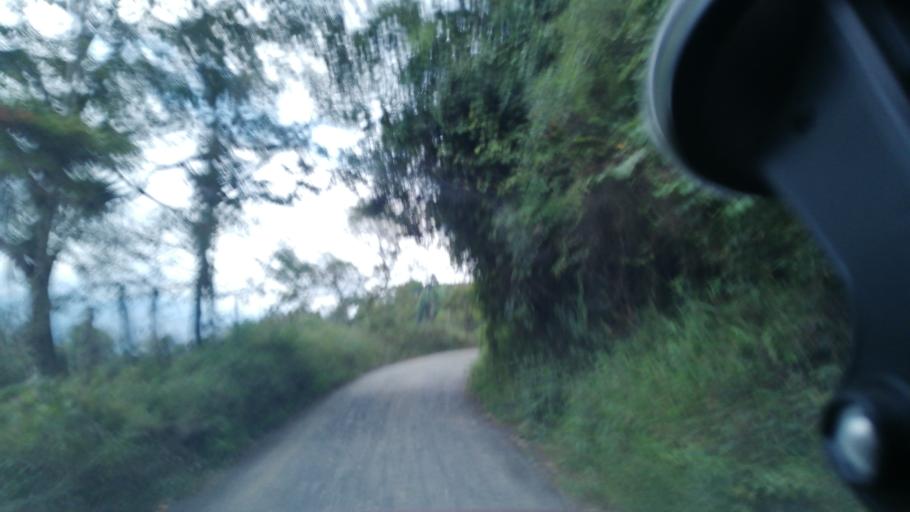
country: CO
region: Cundinamarca
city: Pacho
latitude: 5.1661
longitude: -74.2208
